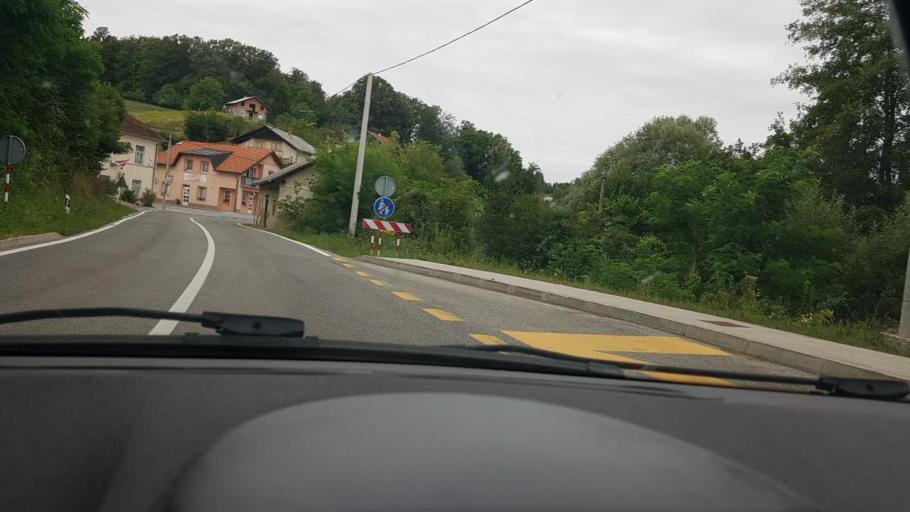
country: SI
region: Rogatec
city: Rogatec
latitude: 46.2066
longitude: 15.6907
